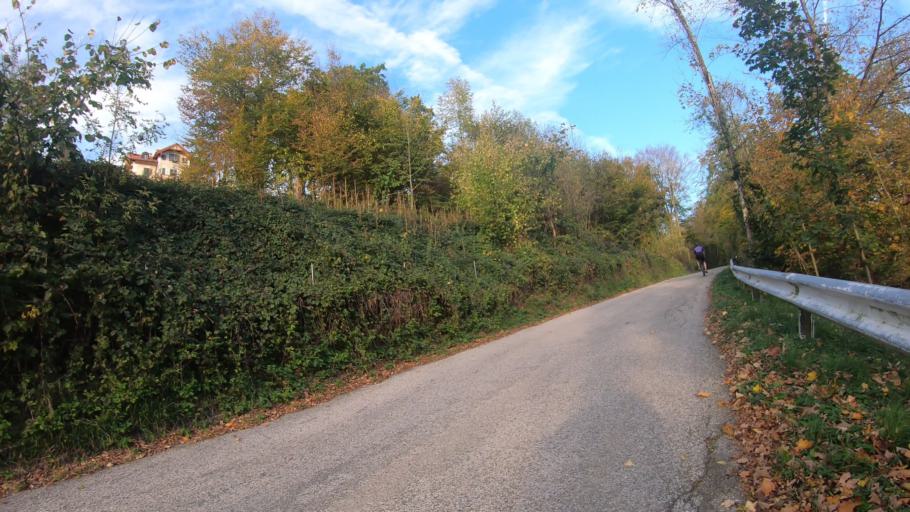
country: DE
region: Bavaria
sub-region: Upper Bavaria
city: Siegsdorf
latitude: 47.8115
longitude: 12.6212
